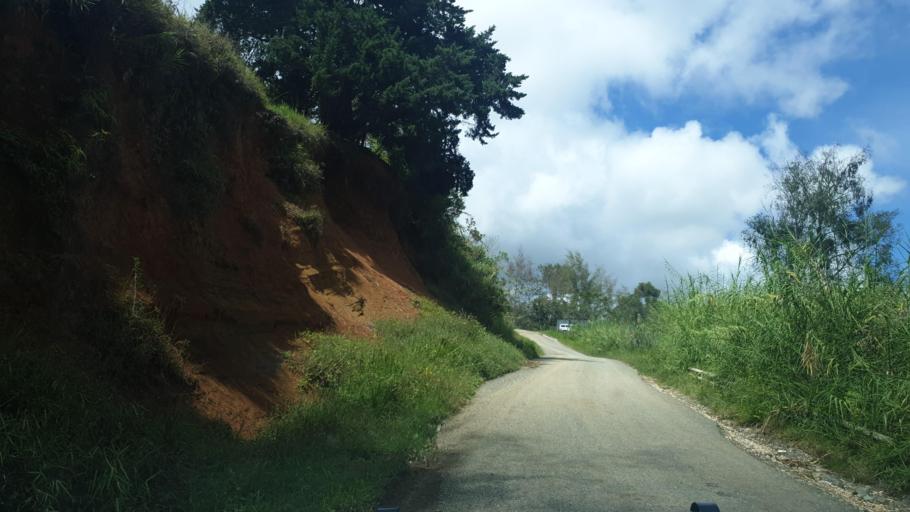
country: PG
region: Chimbu
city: Kundiawa
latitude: -6.1612
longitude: 145.1333
